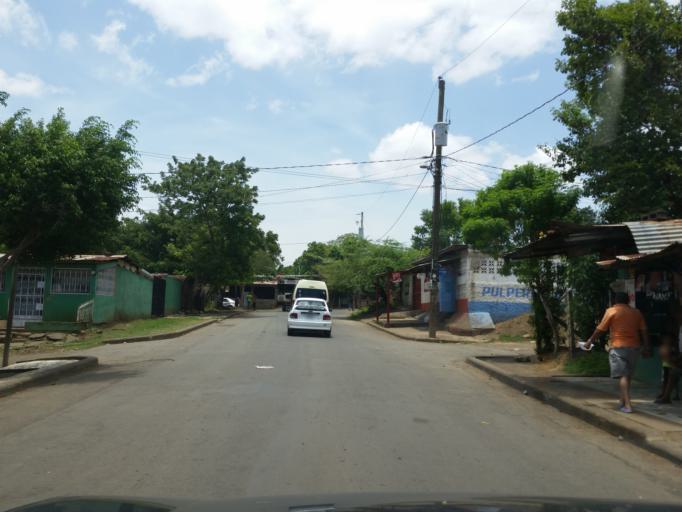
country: NI
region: Managua
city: Managua
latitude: 12.1084
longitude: -86.2378
